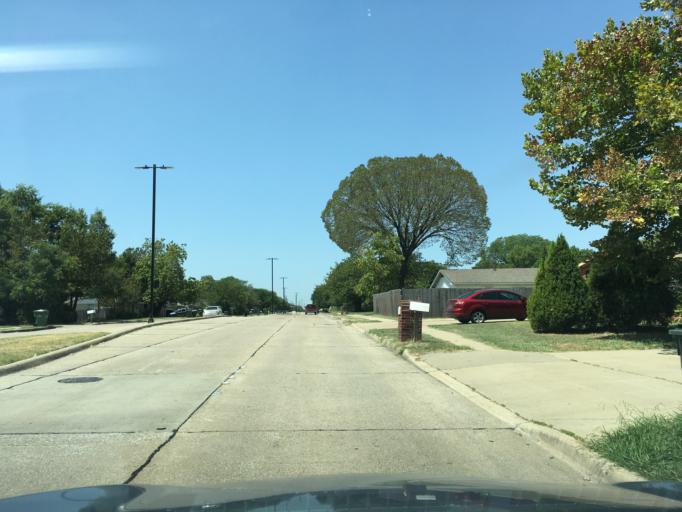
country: US
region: Texas
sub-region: Dallas County
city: Garland
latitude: 32.8943
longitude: -96.6251
